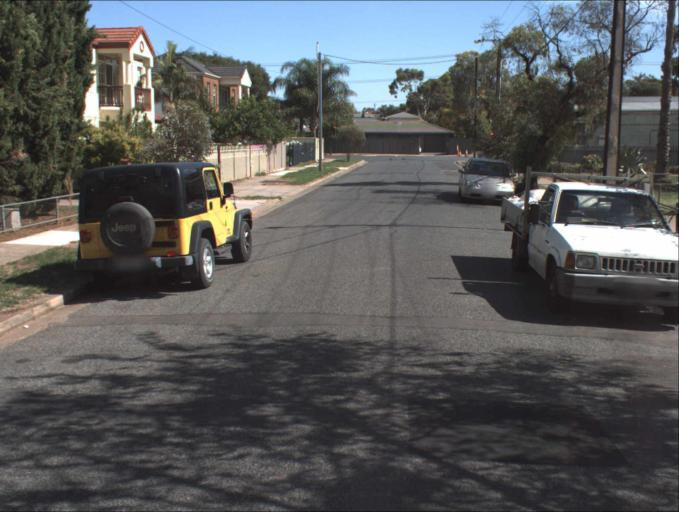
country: AU
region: South Australia
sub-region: Port Adelaide Enfield
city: Klemzig
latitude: -34.8773
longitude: 138.6429
